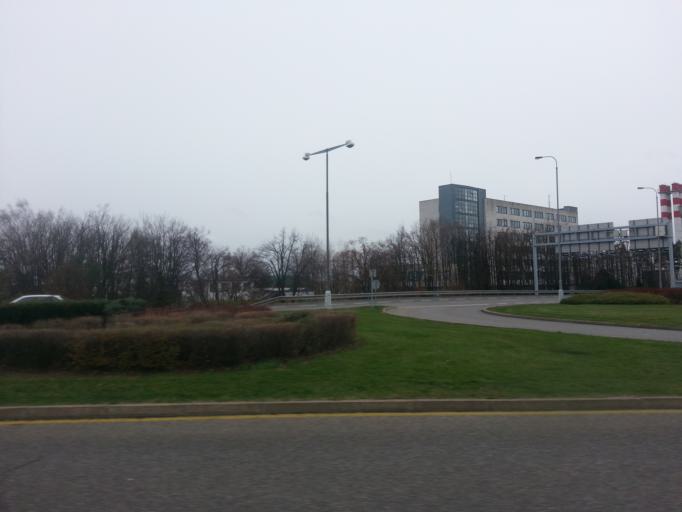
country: CZ
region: Central Bohemia
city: Tuchomerice
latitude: 50.1094
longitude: 14.2732
